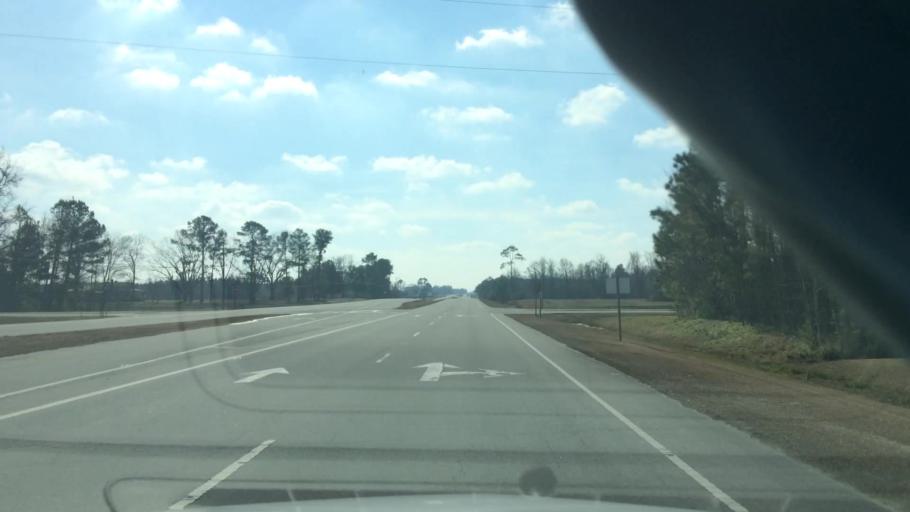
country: US
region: North Carolina
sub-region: Duplin County
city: Beulaville
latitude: 35.1113
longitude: -77.7188
